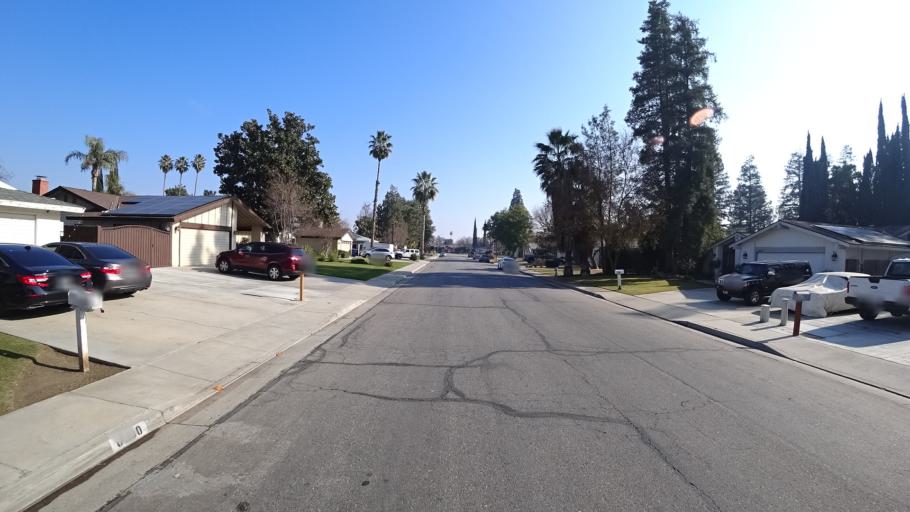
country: US
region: California
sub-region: Kern County
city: Greenacres
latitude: 35.3564
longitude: -119.0768
